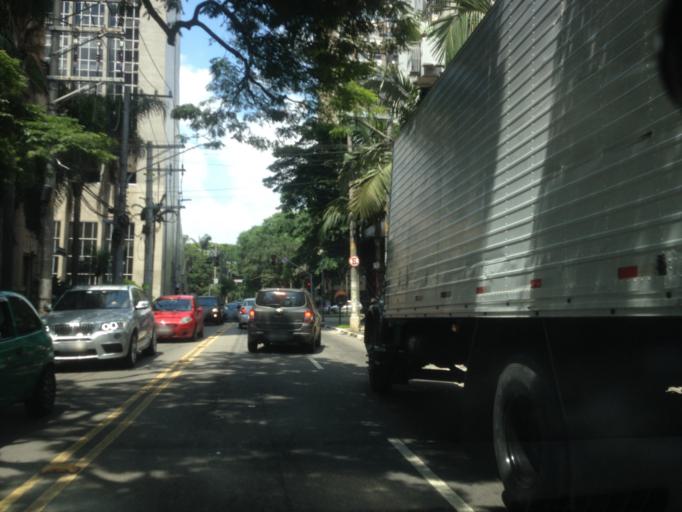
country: BR
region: Sao Paulo
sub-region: Sao Paulo
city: Sao Paulo
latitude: -23.5746
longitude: -46.6878
